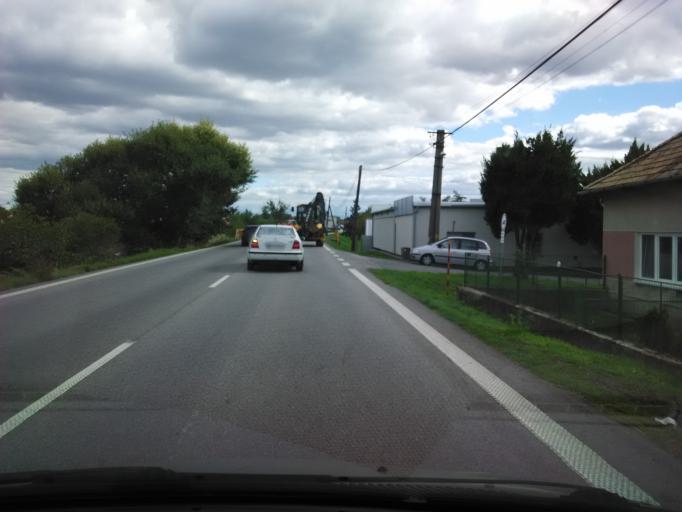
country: SK
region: Nitriansky
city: Levice
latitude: 48.1968
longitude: 18.5400
